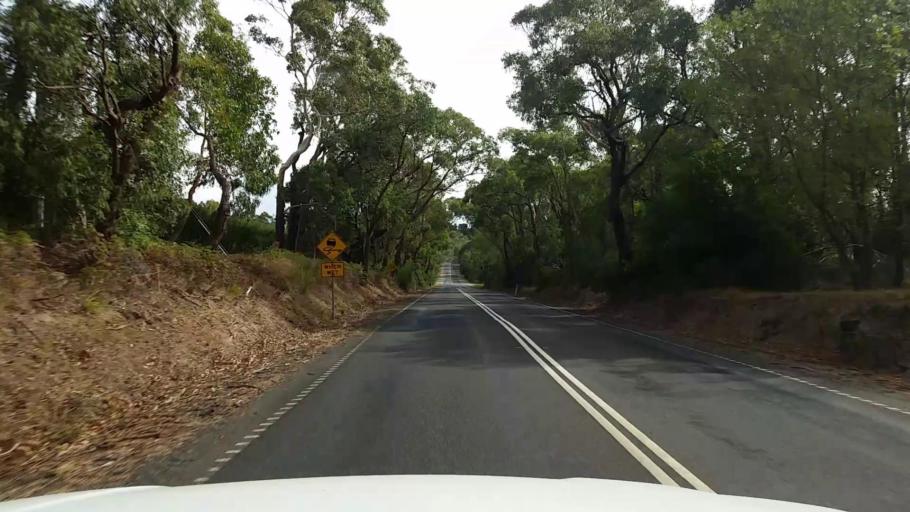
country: AU
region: Victoria
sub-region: Mornington Peninsula
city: Mount Martha
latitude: -38.2974
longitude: 145.0779
